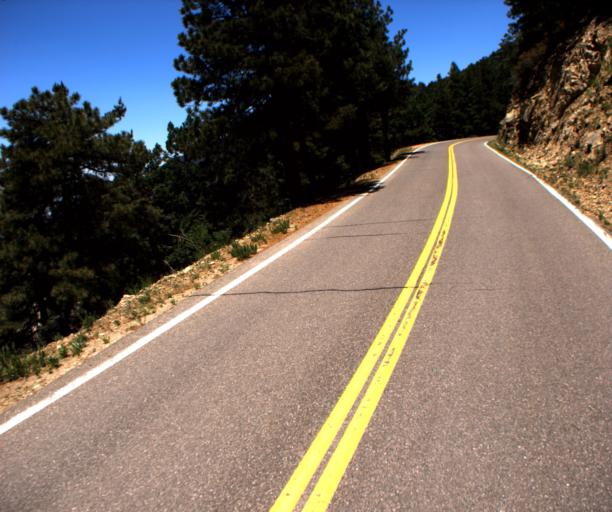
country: US
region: Arizona
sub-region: Graham County
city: Swift Trail Junction
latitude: 32.6381
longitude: -109.8485
